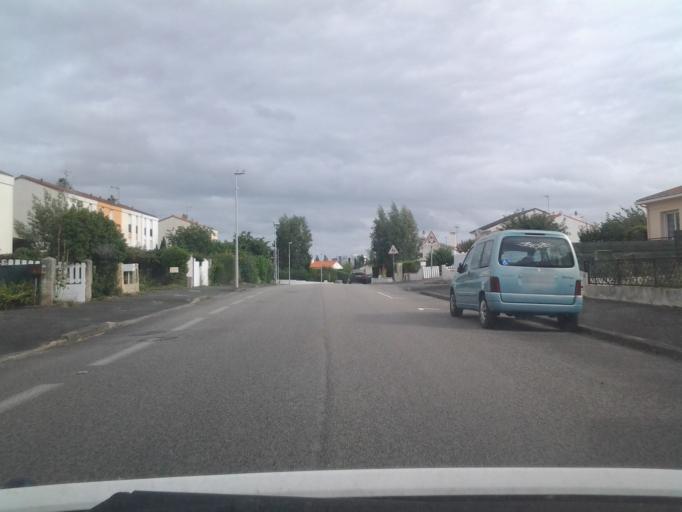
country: FR
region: Pays de la Loire
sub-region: Departement de la Vendee
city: La Roche-sur-Yon
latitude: 46.6842
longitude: -1.4230
